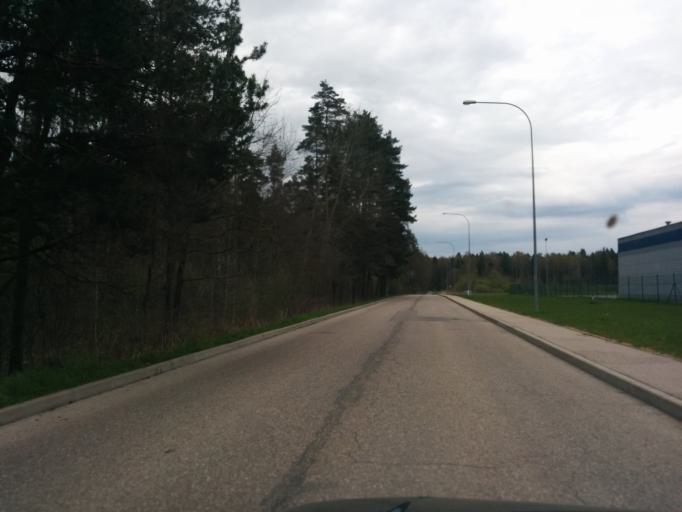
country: LV
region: Ozolnieku
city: Ozolnieki
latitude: 56.6673
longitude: 23.7720
